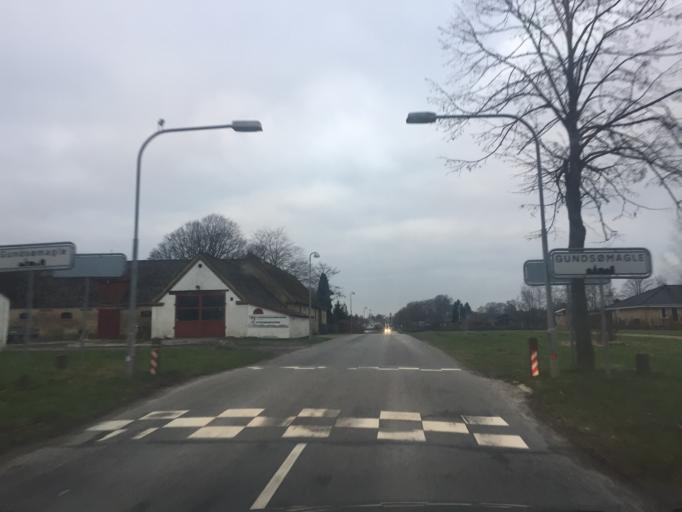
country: DK
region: Zealand
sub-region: Roskilde Kommune
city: Gundsomagle
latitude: 55.7337
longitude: 12.1628
